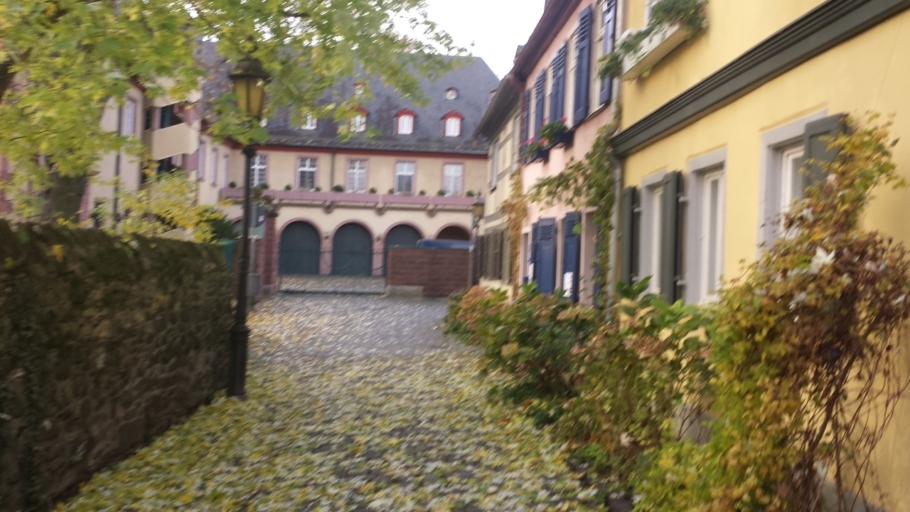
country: DE
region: Hesse
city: Sulzbach
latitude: 50.0984
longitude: 8.5465
